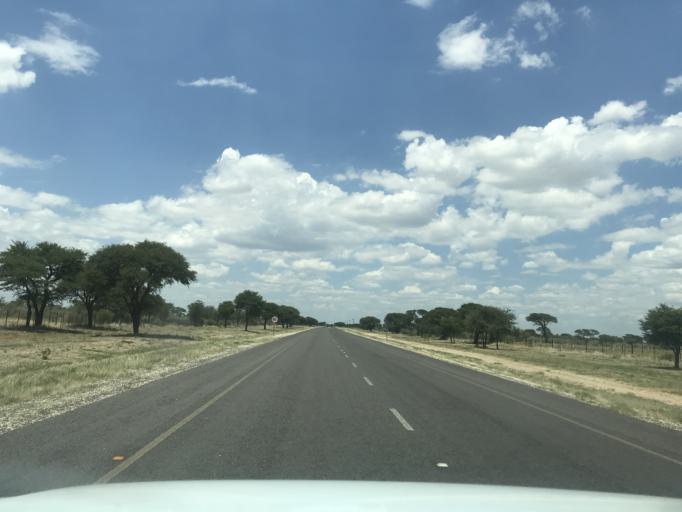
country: BW
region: South East
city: Janeng
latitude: -25.6317
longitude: 25.1545
